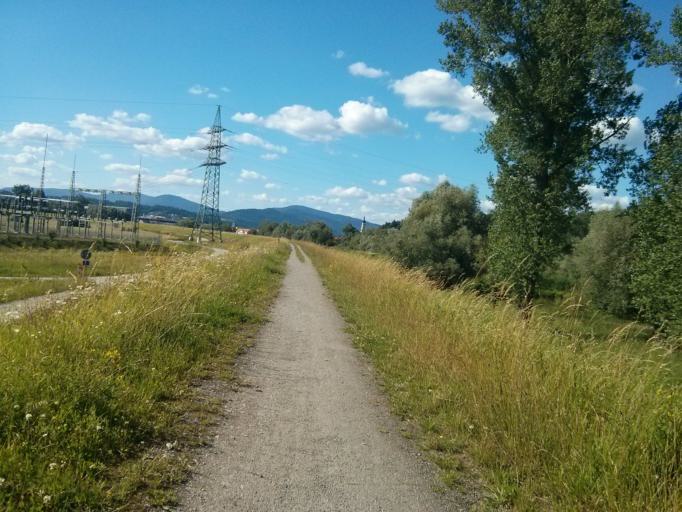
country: DE
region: Bavaria
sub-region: Lower Bavaria
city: Deggendorf
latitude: 48.8165
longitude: 12.9645
